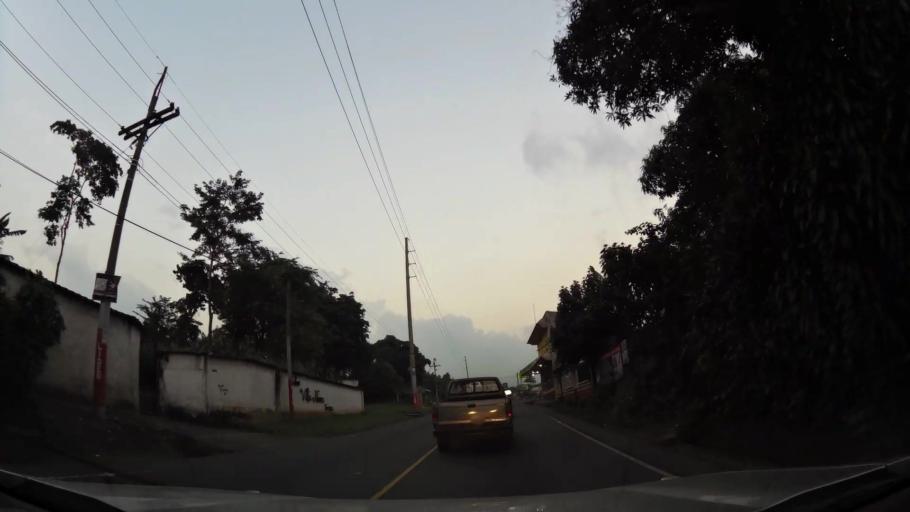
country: GT
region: Retalhuleu
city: San Felipe
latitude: 14.6101
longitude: -91.6058
